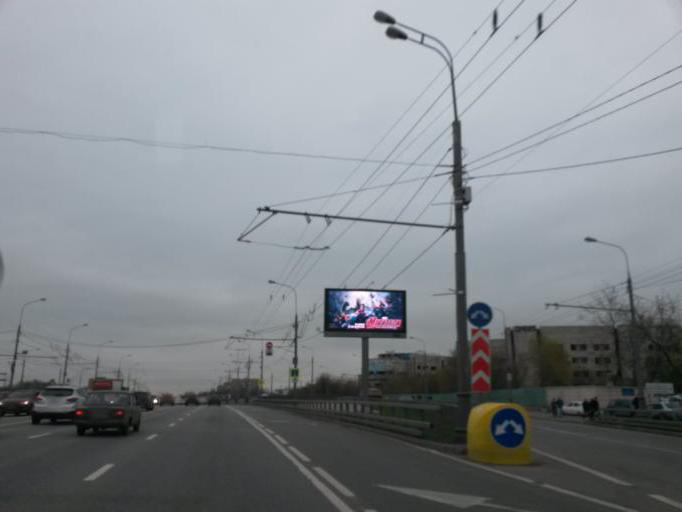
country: RU
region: Moscow
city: Tsaritsyno
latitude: 55.6533
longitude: 37.6525
